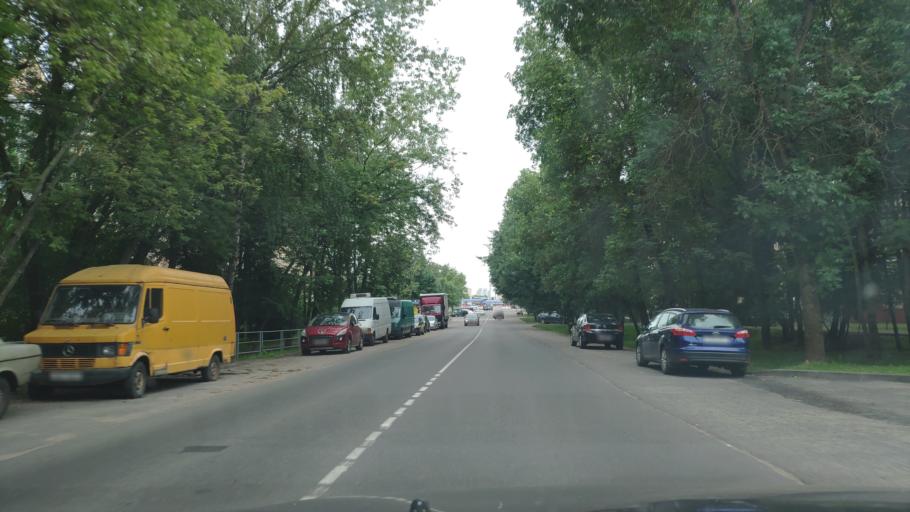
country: BY
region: Minsk
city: Zhdanovichy
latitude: 53.9499
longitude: 27.4286
